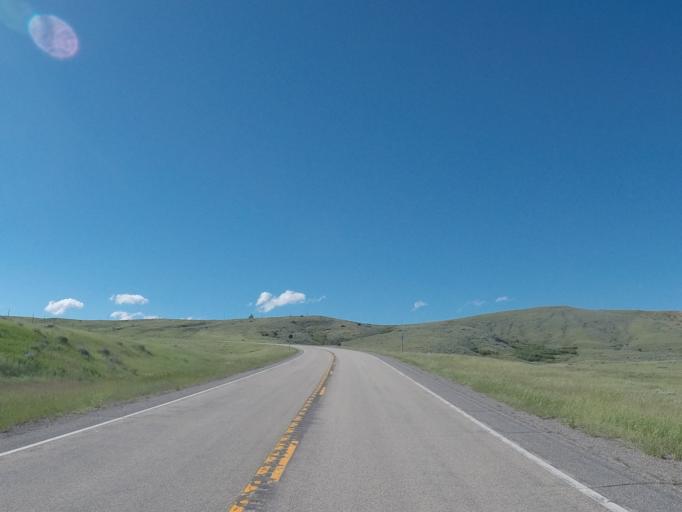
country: US
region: Montana
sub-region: Carbon County
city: Red Lodge
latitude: 45.1746
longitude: -109.2104
